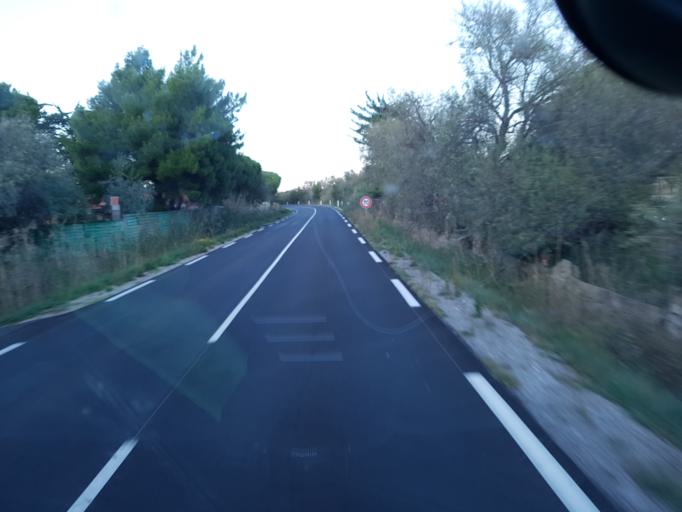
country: FR
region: Languedoc-Roussillon
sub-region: Departement de l'Aude
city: Port-la-Nouvelle
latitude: 42.9955
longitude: 3.0408
